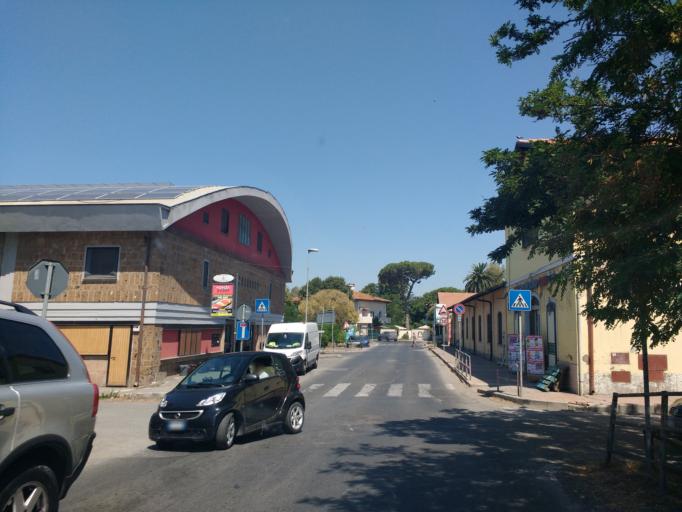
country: IT
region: Latium
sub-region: Citta metropolitana di Roma Capitale
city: Maccarese
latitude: 41.8769
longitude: 12.2150
